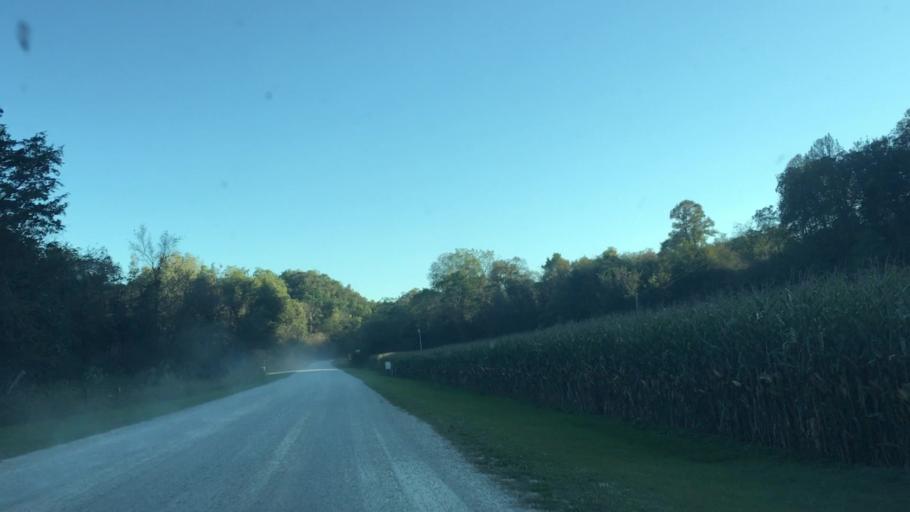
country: US
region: Minnesota
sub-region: Fillmore County
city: Preston
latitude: 43.7584
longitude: -92.0300
